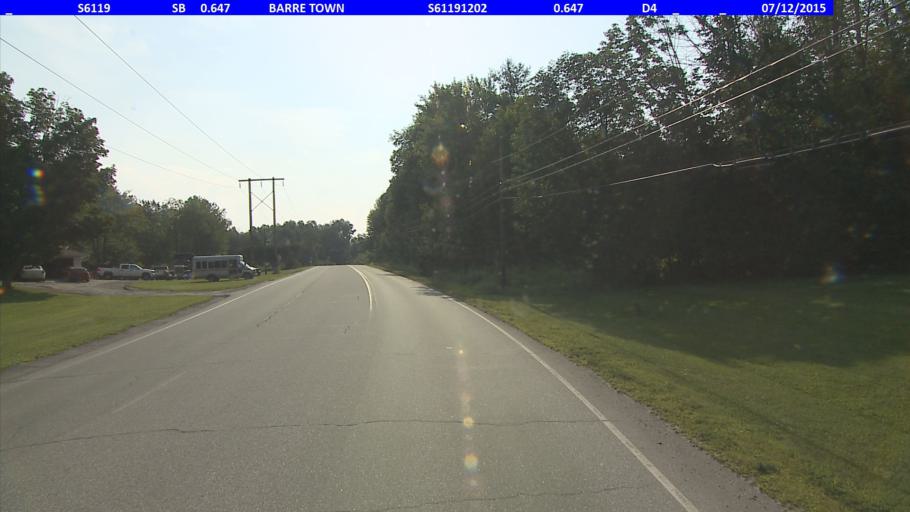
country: US
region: Vermont
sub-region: Washington County
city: South Barre
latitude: 44.1769
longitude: -72.4945
